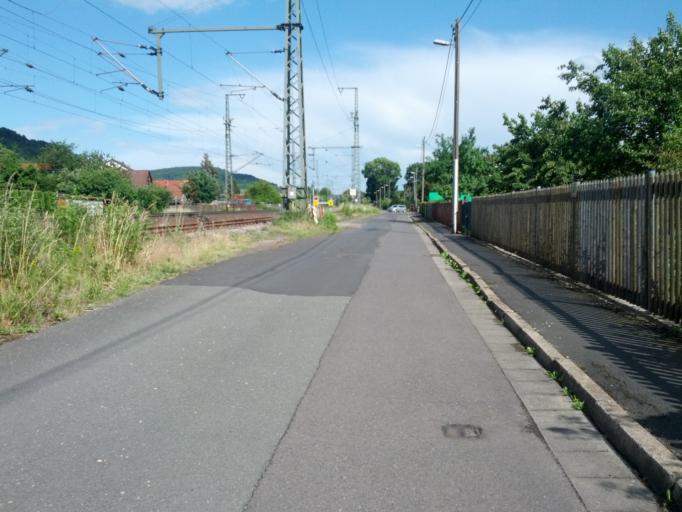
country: DE
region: Thuringia
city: Eisenach
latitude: 50.9670
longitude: 10.3550
